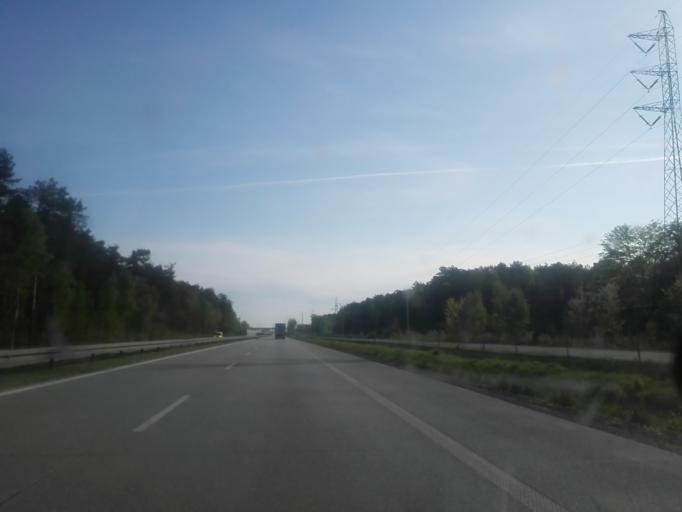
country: PL
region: Lodz Voivodeship
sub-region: Powiat piotrkowski
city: Moszczenica
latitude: 51.4533
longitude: 19.7705
